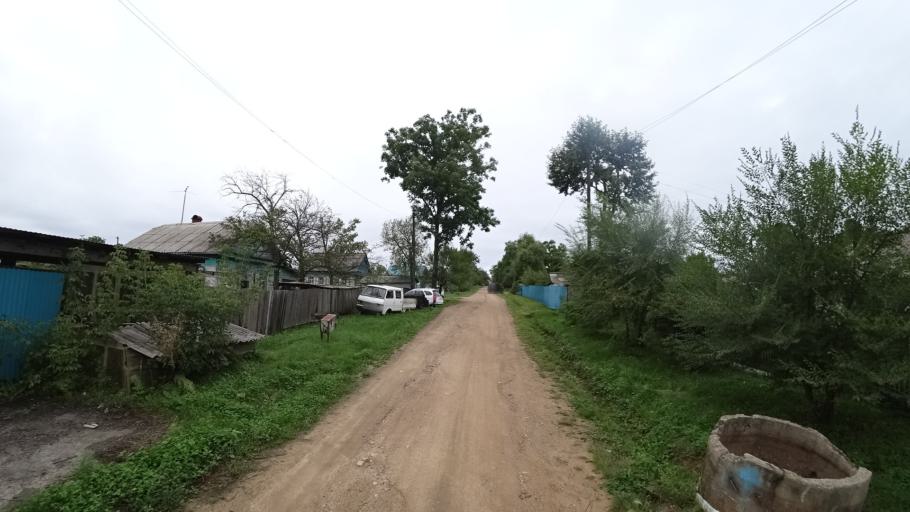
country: RU
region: Primorskiy
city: Rettikhovka
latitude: 44.1682
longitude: 132.7687
